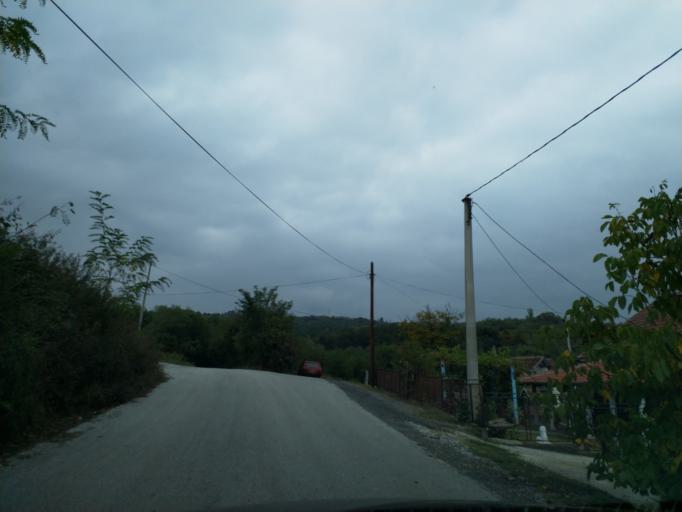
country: RS
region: Central Serbia
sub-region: Sumadijski Okrug
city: Arangelovac
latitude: 44.3098
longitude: 20.5912
